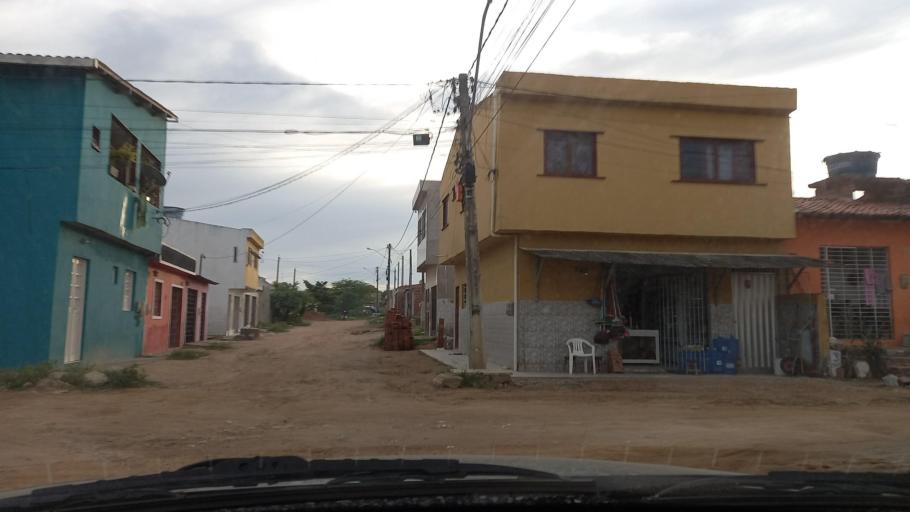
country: BR
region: Pernambuco
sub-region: Gravata
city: Gravata
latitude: -8.1929
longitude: -35.5799
